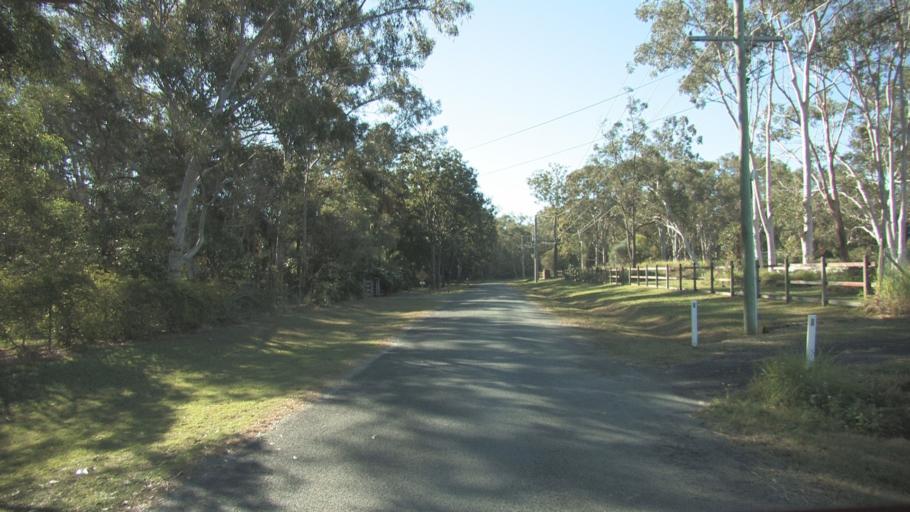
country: AU
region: Queensland
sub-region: Logan
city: Logan Reserve
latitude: -27.7300
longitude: 153.0832
